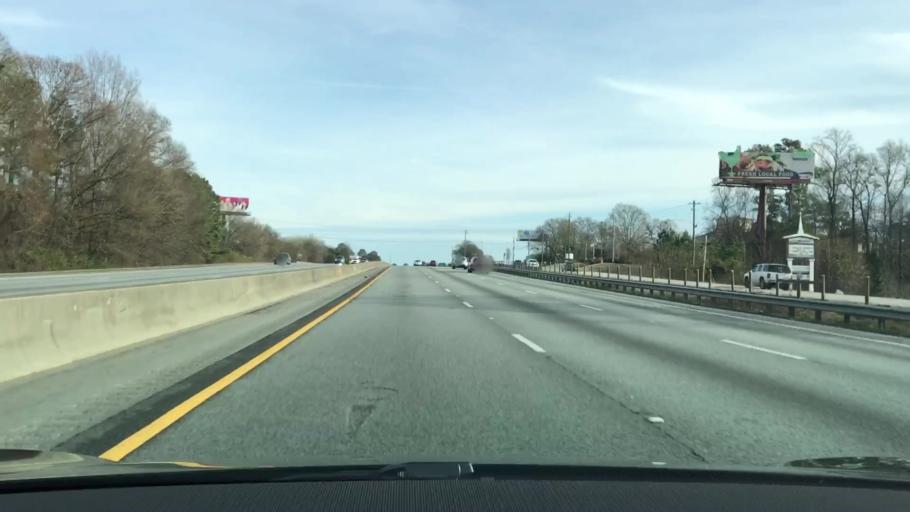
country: US
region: Georgia
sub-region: Newton County
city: Oxford
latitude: 33.6100
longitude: -83.8856
